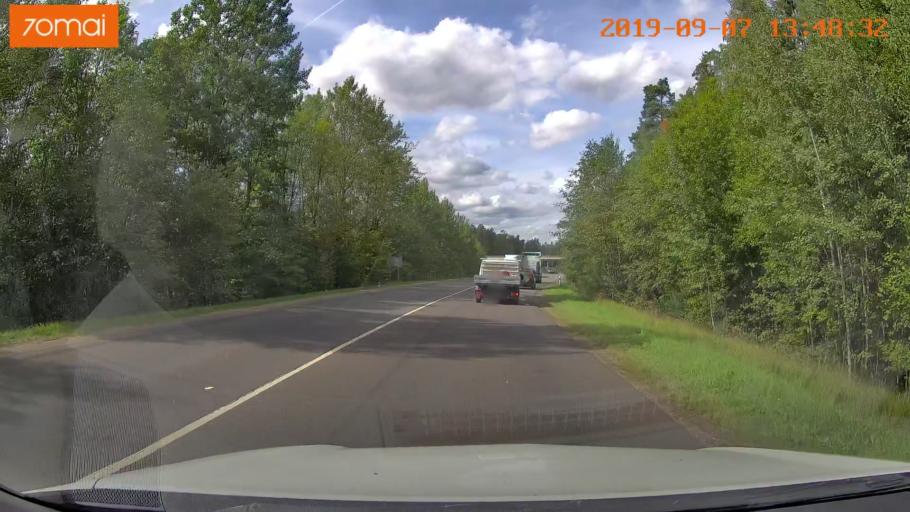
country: LT
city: Baltoji Voke
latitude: 54.6023
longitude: 25.2014
